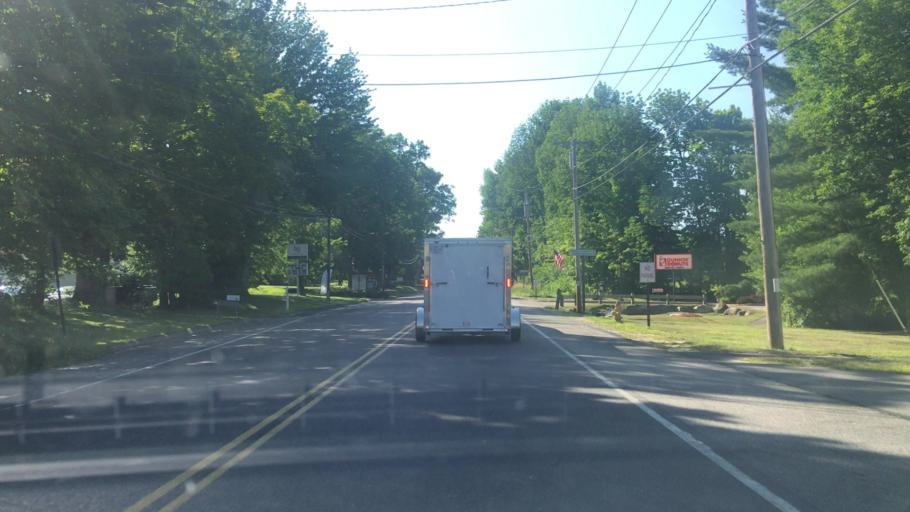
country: US
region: Maine
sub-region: York County
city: Buxton
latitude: 43.7334
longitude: -70.5466
